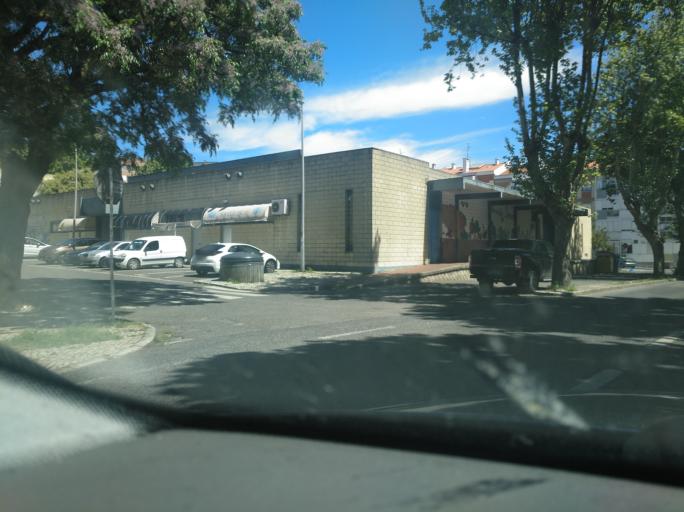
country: PT
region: Lisbon
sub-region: Amadora
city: Amadora
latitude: 38.7409
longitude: -9.2105
